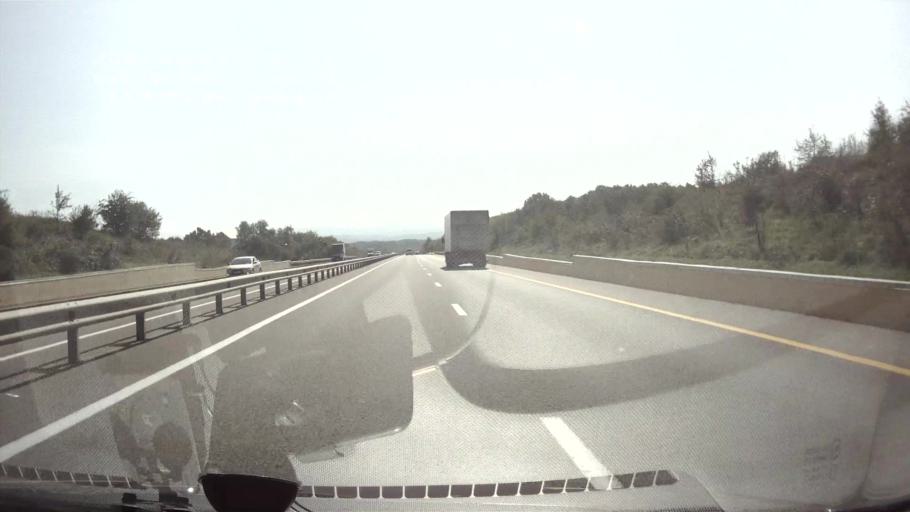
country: RU
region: Krasnodarskiy
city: Saratovskaya
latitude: 44.7056
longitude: 39.2044
